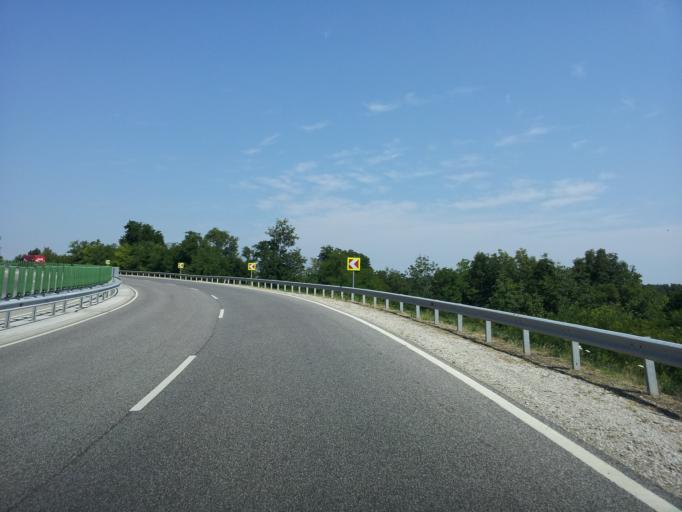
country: HU
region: Zala
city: Pacsa
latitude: 46.8286
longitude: 16.9720
